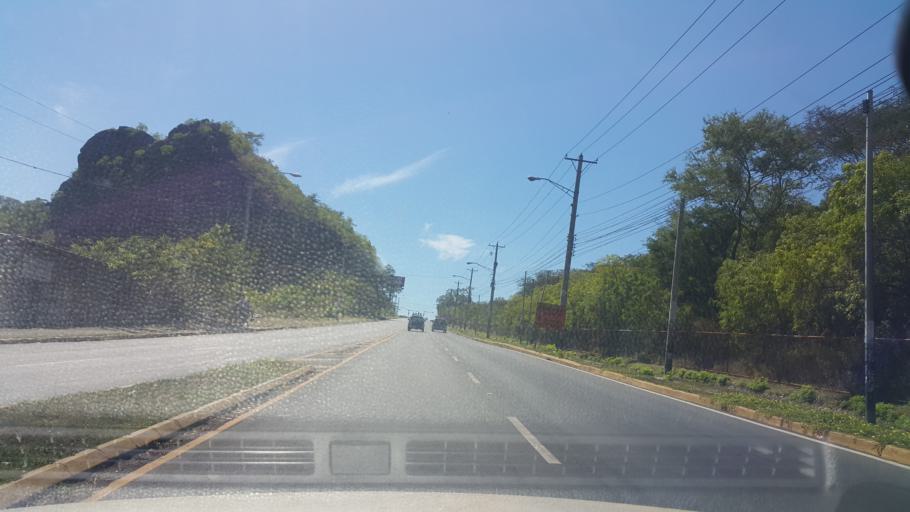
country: NI
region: Managua
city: Ciudad Sandino
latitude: 12.1364
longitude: -86.3085
